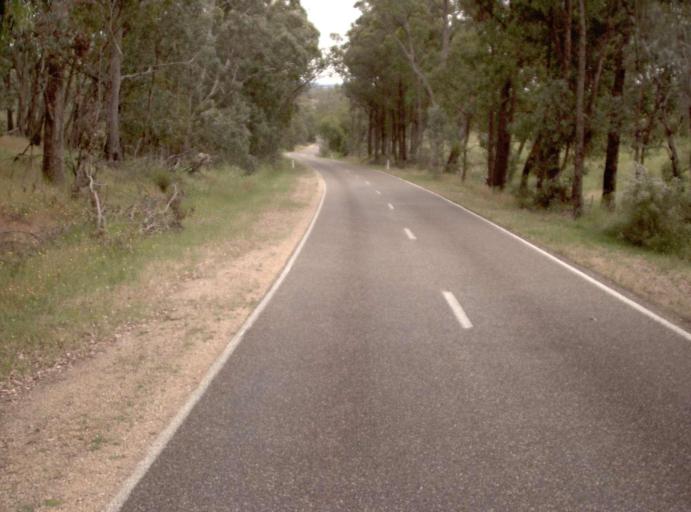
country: AU
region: Victoria
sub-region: East Gippsland
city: Bairnsdale
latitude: -37.7837
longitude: 147.3242
